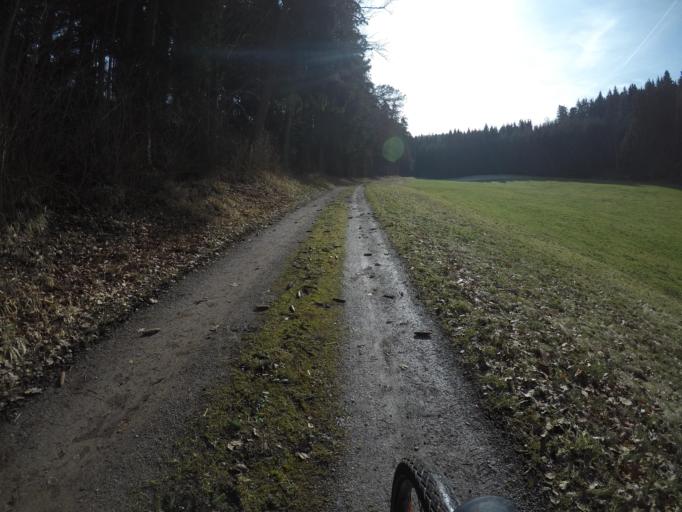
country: DE
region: Baden-Wuerttemberg
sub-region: Regierungsbezirk Stuttgart
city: Oberjettingen
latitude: 48.5991
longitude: 8.7900
